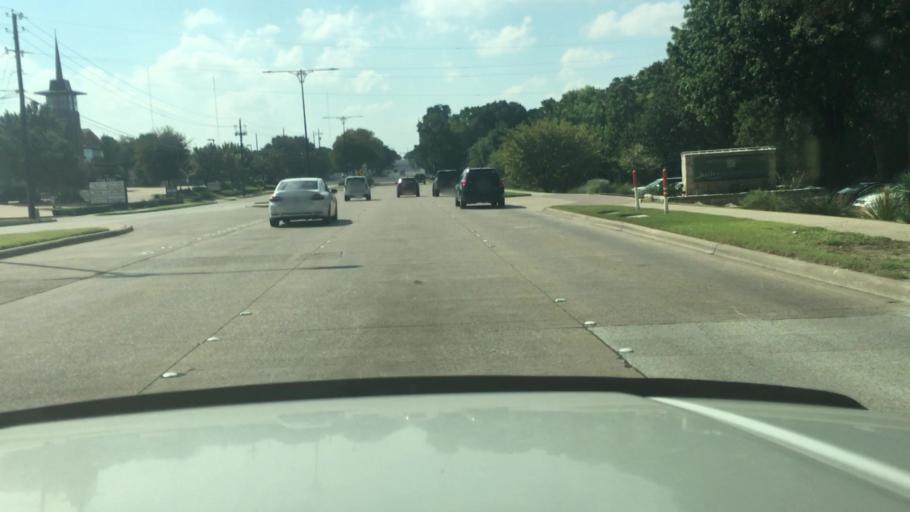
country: US
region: Texas
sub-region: Dallas County
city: Coppell
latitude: 32.9588
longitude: -96.9936
